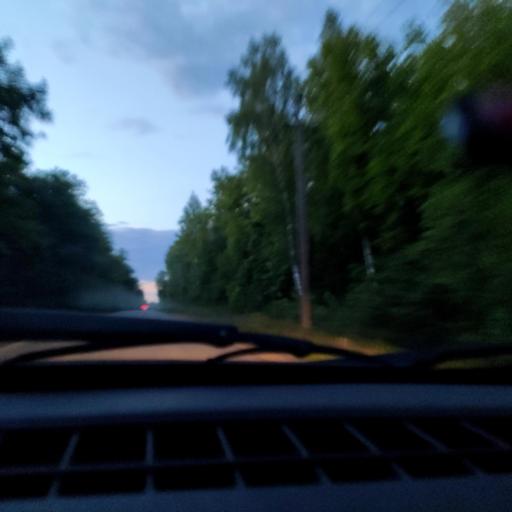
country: RU
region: Bashkortostan
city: Avdon
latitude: 54.6495
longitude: 55.5799
